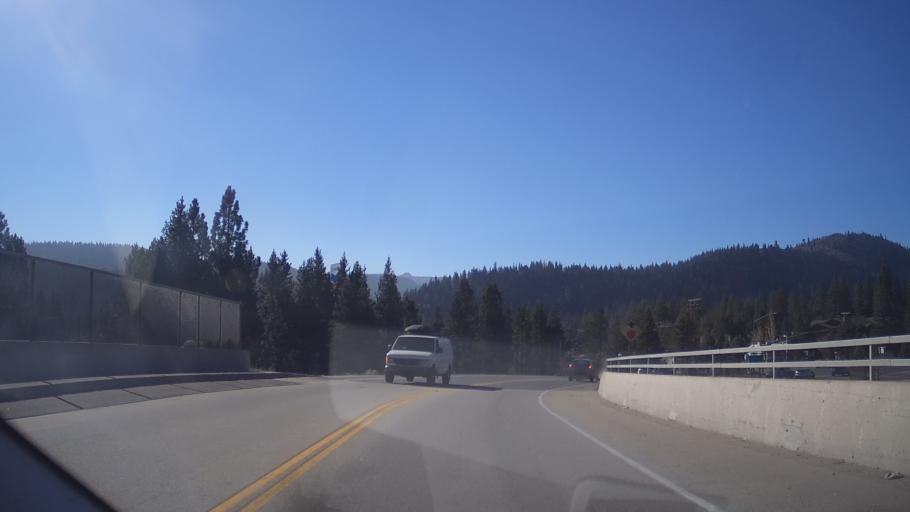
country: US
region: California
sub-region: Nevada County
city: Truckee
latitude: 39.3243
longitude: -120.2258
